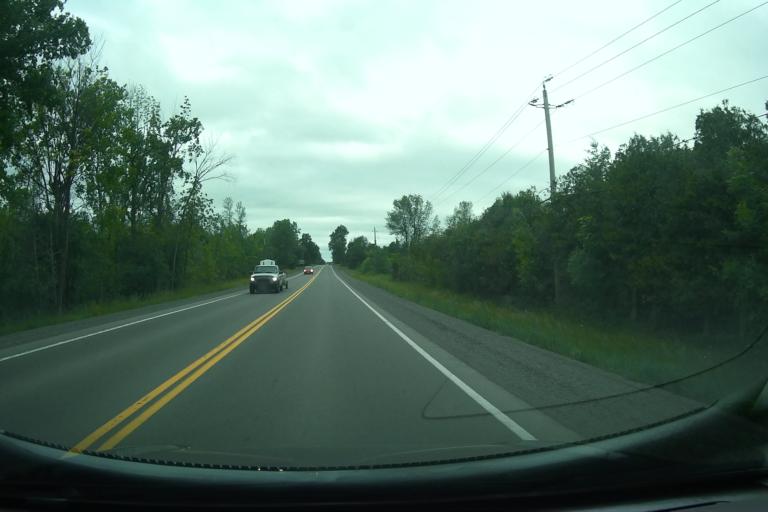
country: CA
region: Ontario
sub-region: Lanark County
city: Smiths Falls
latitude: 44.9875
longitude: -75.7177
